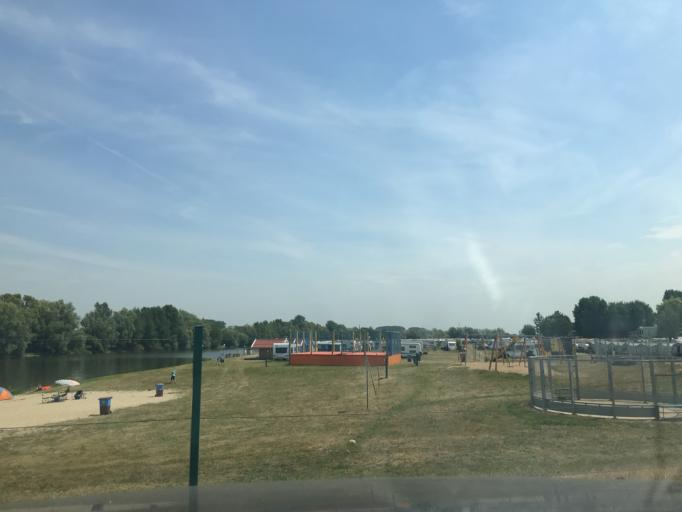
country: DE
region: North Rhine-Westphalia
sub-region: Regierungsbezirk Dusseldorf
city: Wesel
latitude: 51.6685
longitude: 6.5561
